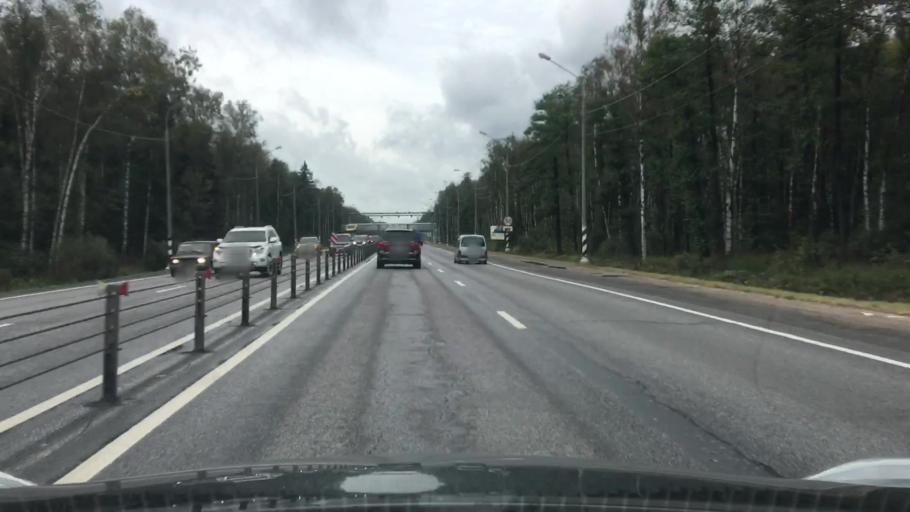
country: RU
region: Moskovskaya
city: Reshetnikovo
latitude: 56.4062
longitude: 36.6473
